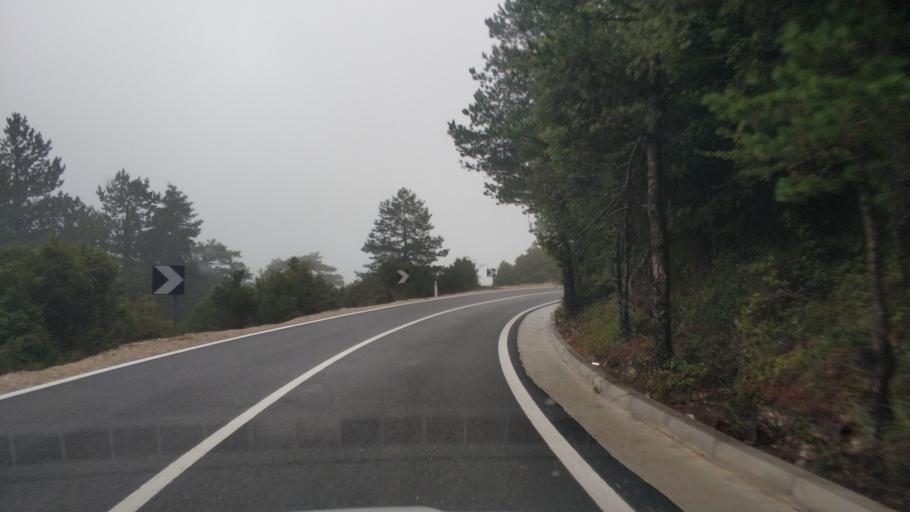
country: AL
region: Vlore
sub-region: Rrethi i Vlores
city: Vranisht
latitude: 40.2025
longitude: 19.5883
